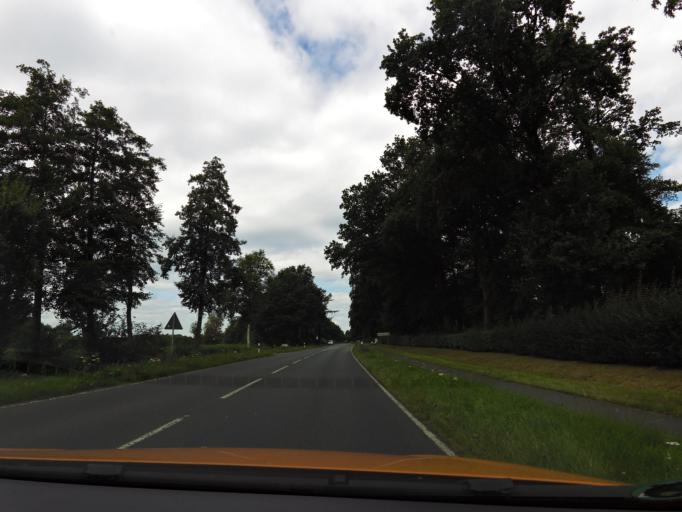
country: DE
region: Lower Saxony
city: Oldenburg
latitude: 53.1684
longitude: 8.1394
